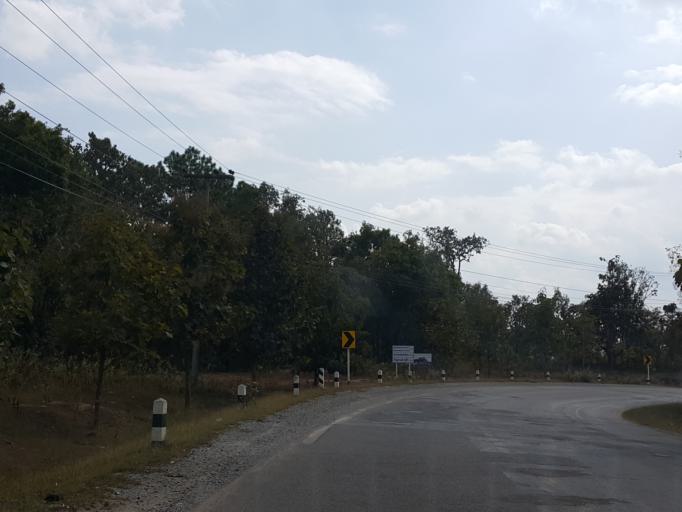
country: TH
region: Chiang Mai
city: Om Koi
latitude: 17.8410
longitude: 98.3740
